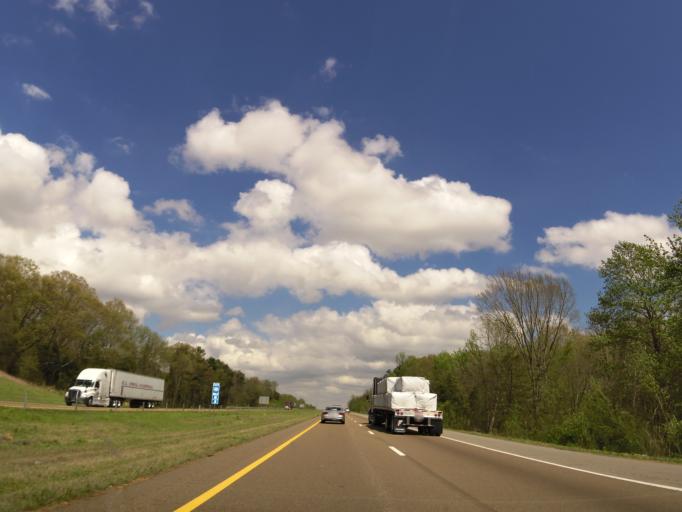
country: US
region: Tennessee
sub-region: Shelby County
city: Arlington
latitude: 35.2738
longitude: -89.6427
